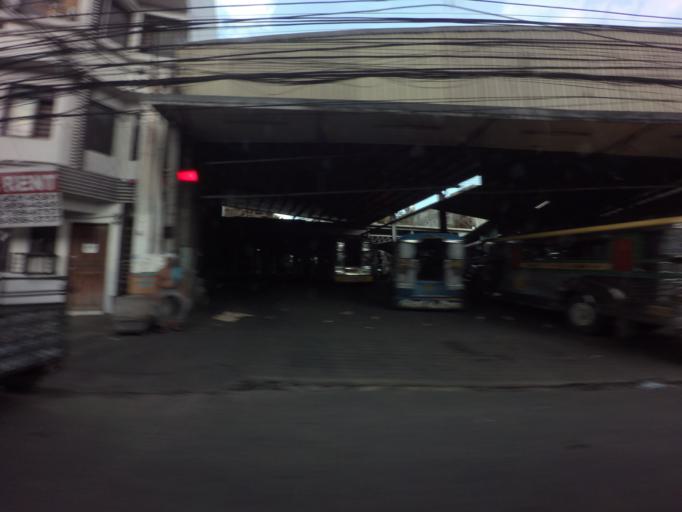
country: PH
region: Metro Manila
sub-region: Mandaluyong
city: Mandaluyong City
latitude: 14.5653
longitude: 121.0475
